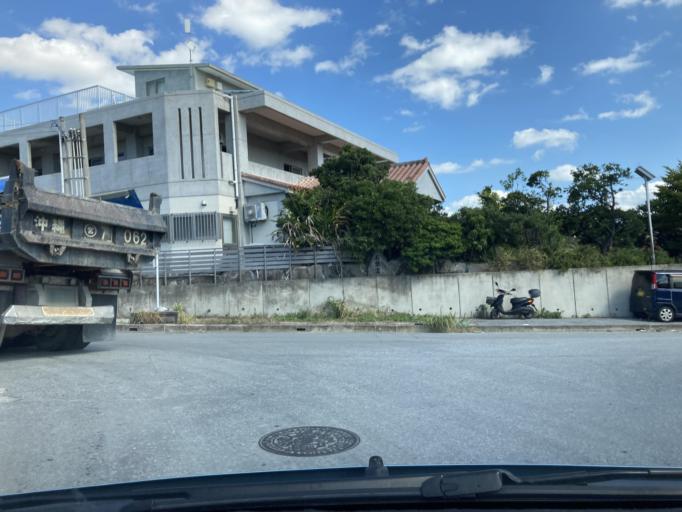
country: JP
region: Okinawa
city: Tomigusuku
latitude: 26.1882
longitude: 127.7126
